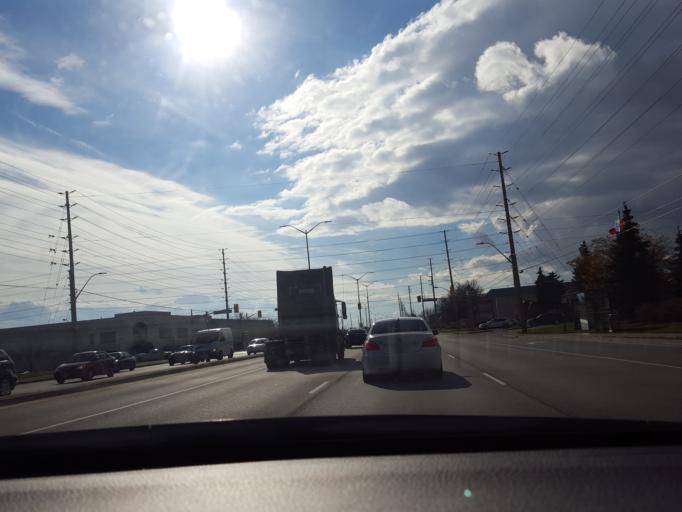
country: CA
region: Ontario
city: Brampton
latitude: 43.6725
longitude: -79.6774
